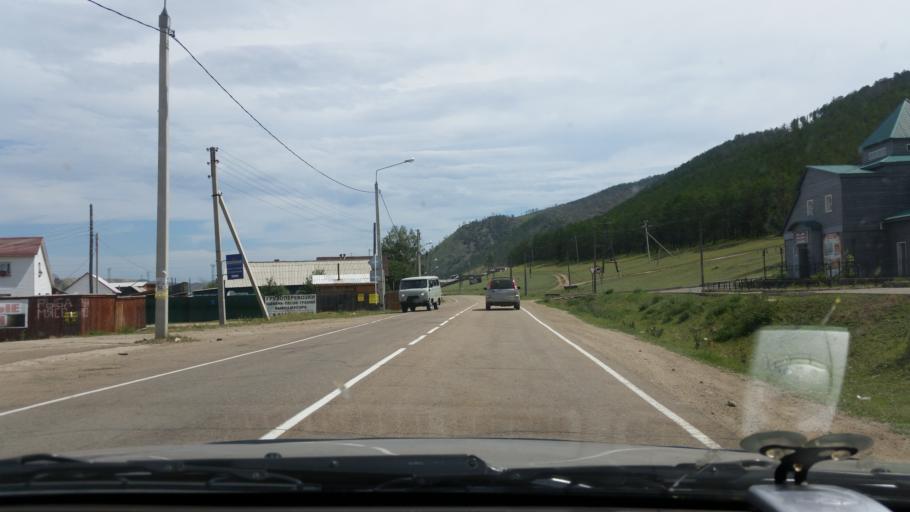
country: RU
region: Irkutsk
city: Yelantsy
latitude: 52.7932
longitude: 106.3923
